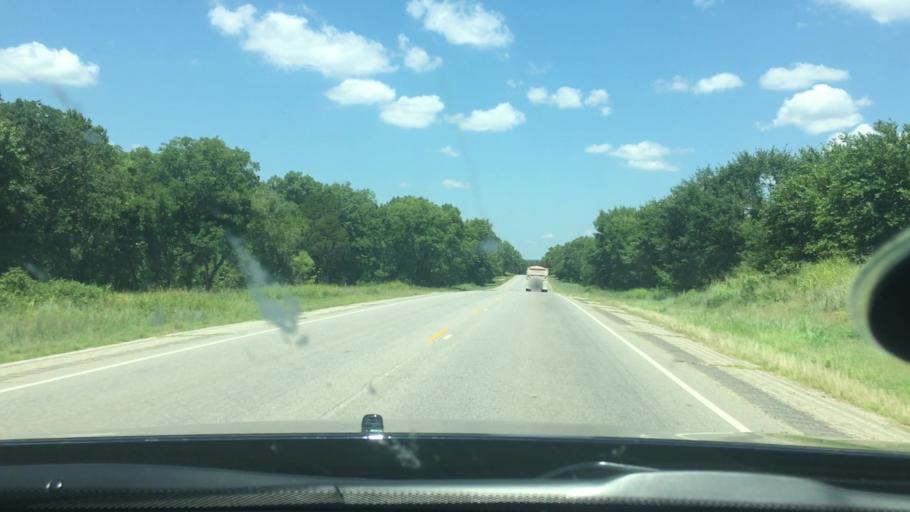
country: US
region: Oklahoma
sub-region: Marshall County
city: Oakland
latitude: 34.1611
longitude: -96.8245
